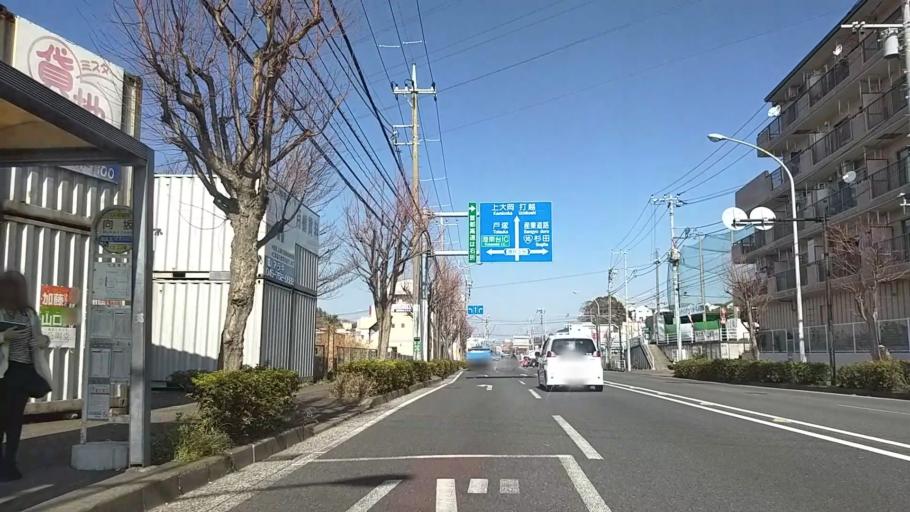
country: JP
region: Kanagawa
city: Yokohama
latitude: 35.3760
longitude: 139.6099
